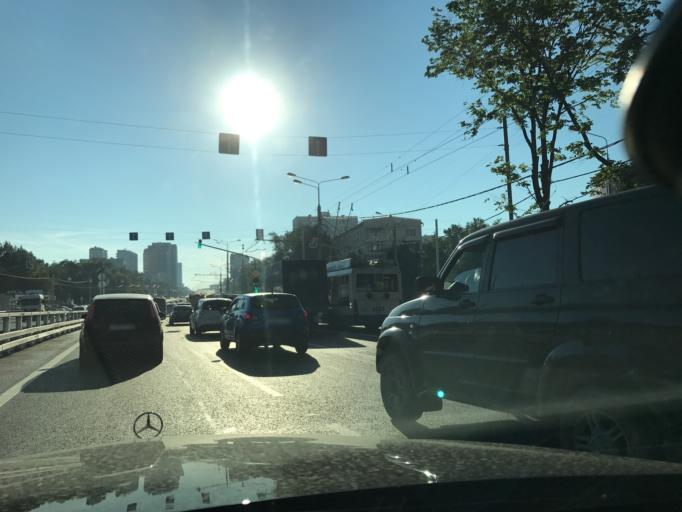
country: RU
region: Moscow
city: Metrogorodok
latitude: 55.8096
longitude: 37.7803
